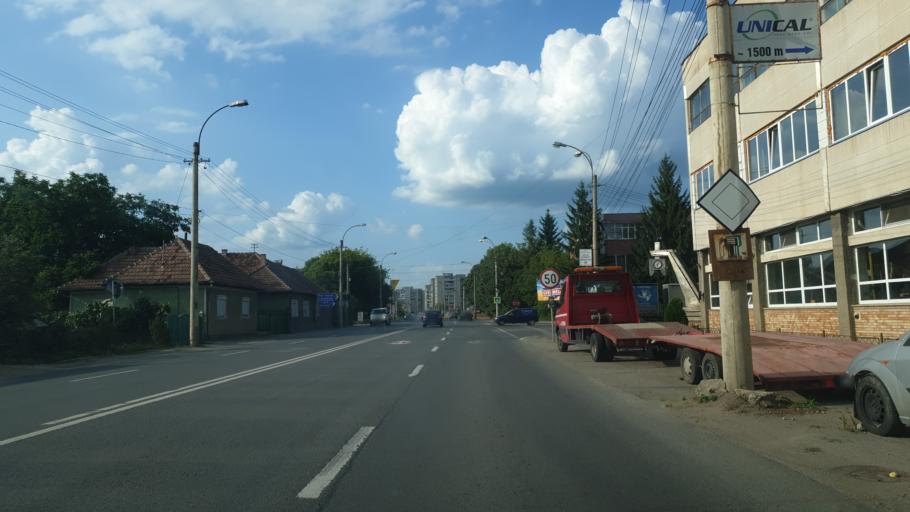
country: RO
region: Covasna
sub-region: Municipiul Sfantu Gheorghe
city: Sfantu-Gheorghe
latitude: 45.8556
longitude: 25.8069
